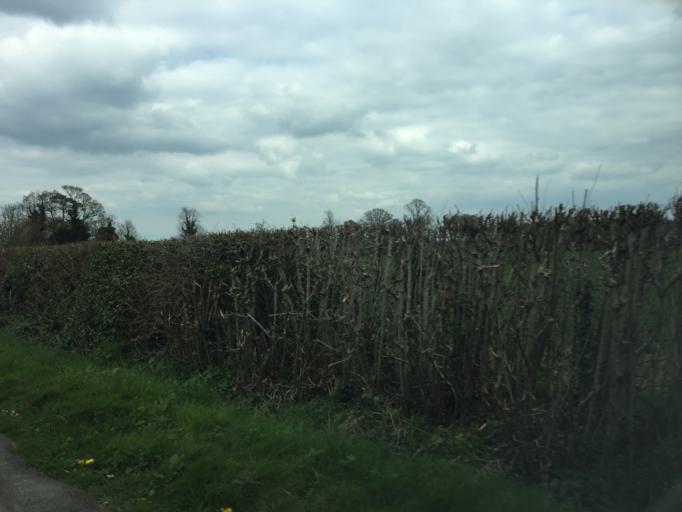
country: GB
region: England
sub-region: Oxfordshire
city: Bicester
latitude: 51.9382
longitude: -1.1370
